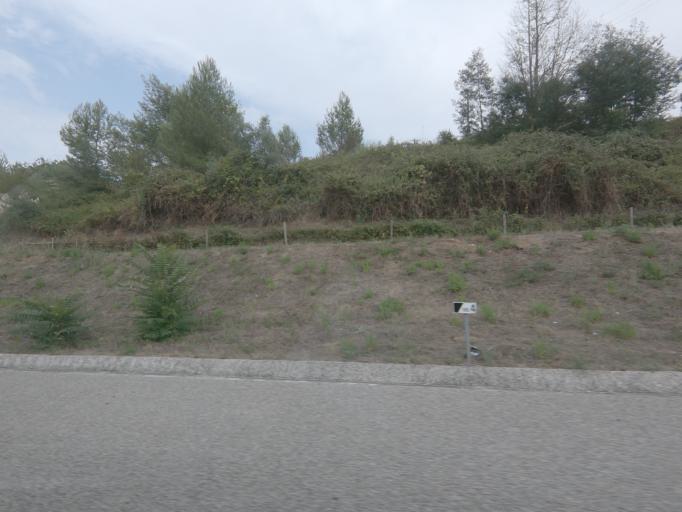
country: PT
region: Coimbra
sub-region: Coimbra
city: Coimbra
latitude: 40.2103
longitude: -8.4462
